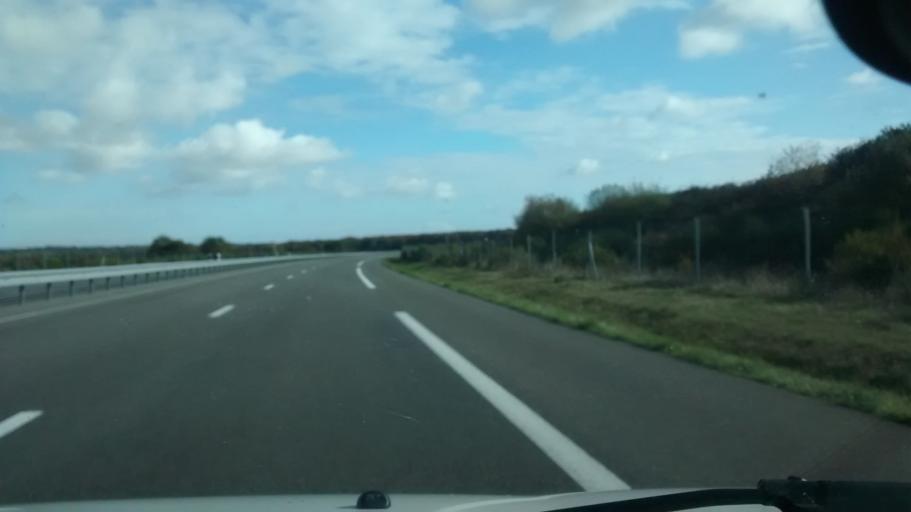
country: FR
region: Pays de la Loire
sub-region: Departement de Maine-et-Loire
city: Combree
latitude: 47.7304
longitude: -1.0838
